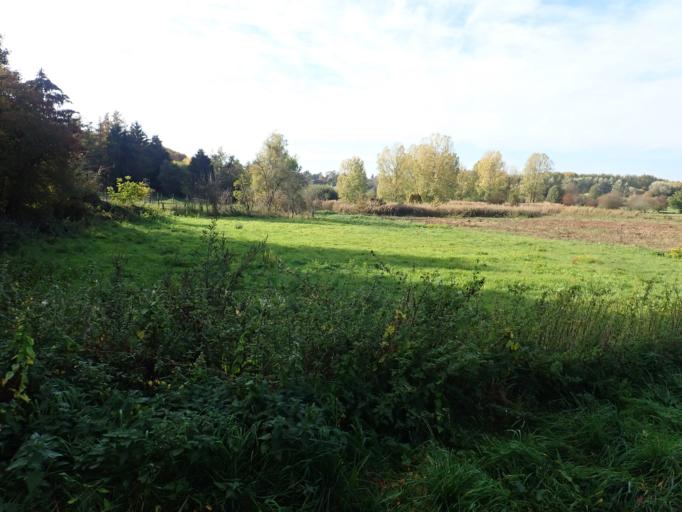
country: BE
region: Flanders
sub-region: Provincie Vlaams-Brabant
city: Diest
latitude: 50.9874
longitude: 5.0153
